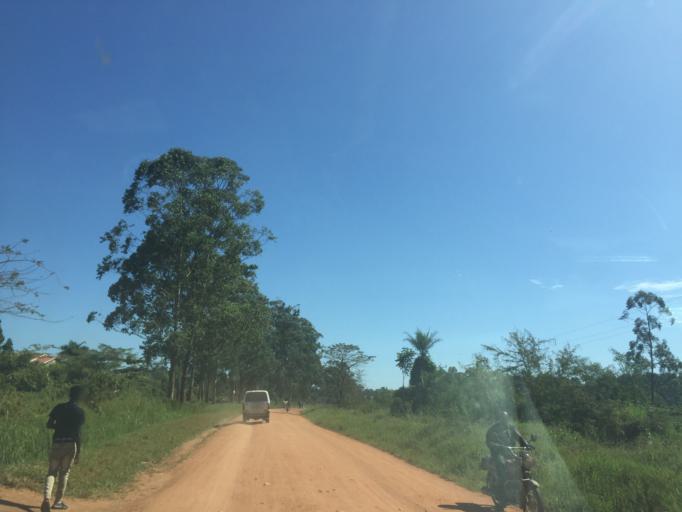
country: UG
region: Central Region
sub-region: Luwero District
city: Luwero
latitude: 0.8436
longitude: 32.5084
